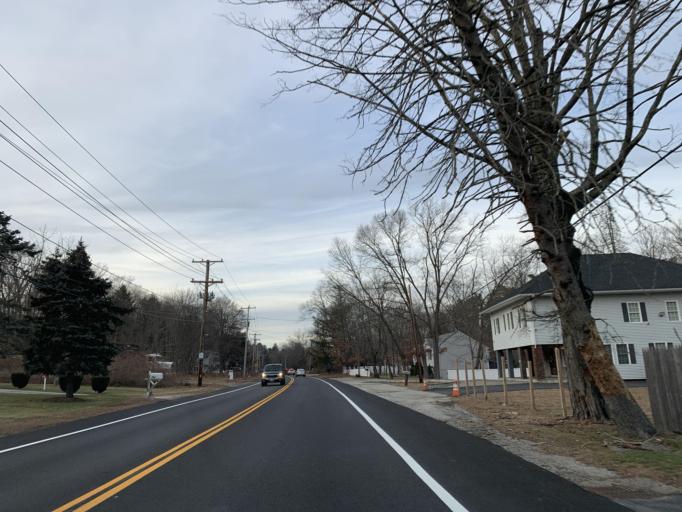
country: US
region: Rhode Island
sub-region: Providence County
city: Greenville
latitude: 41.8580
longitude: -71.5274
